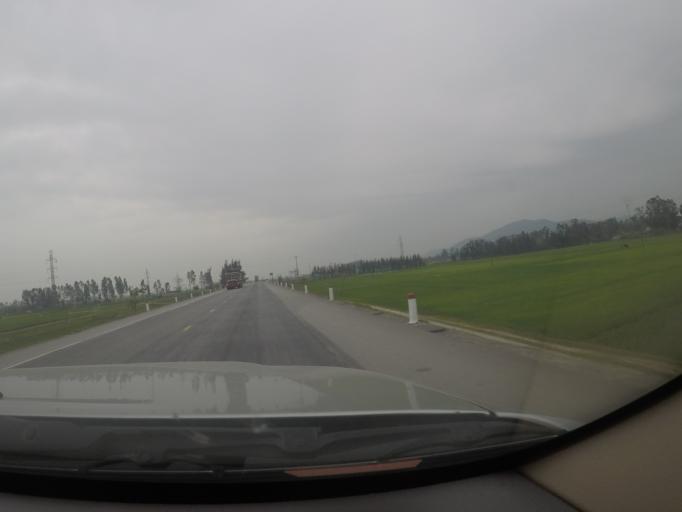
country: VN
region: Nghe An
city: Quan Hanh
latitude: 18.7617
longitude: 105.6321
